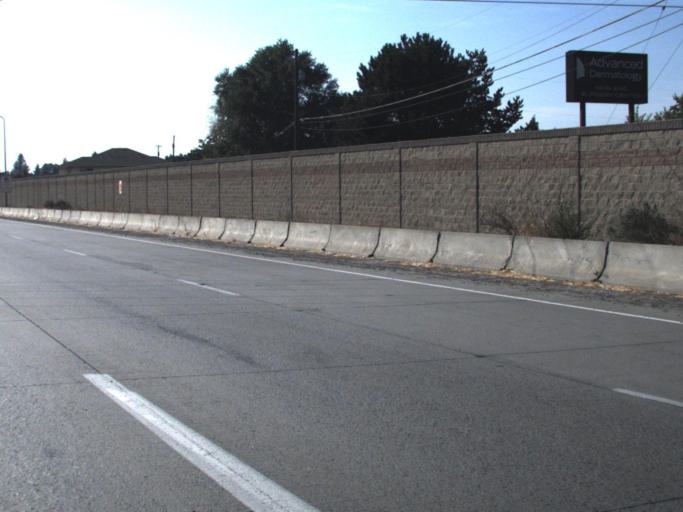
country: US
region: Washington
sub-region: Spokane County
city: Millwood
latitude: 47.6730
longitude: -117.2880
